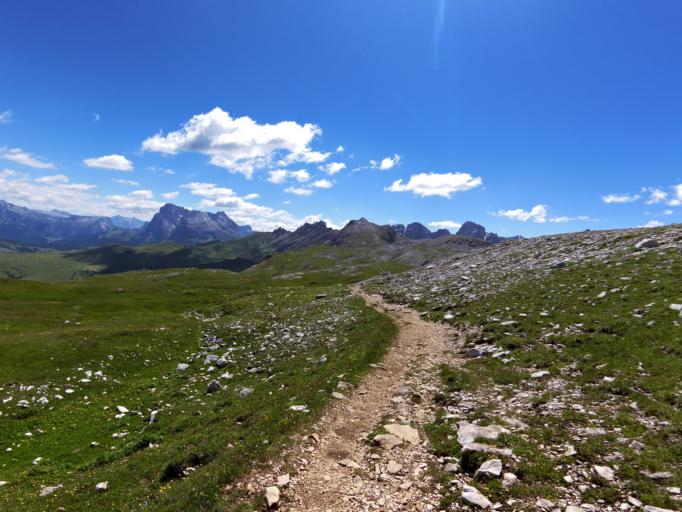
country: IT
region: Trentino-Alto Adige
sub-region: Bolzano
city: Siusi
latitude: 46.5077
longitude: 11.5834
